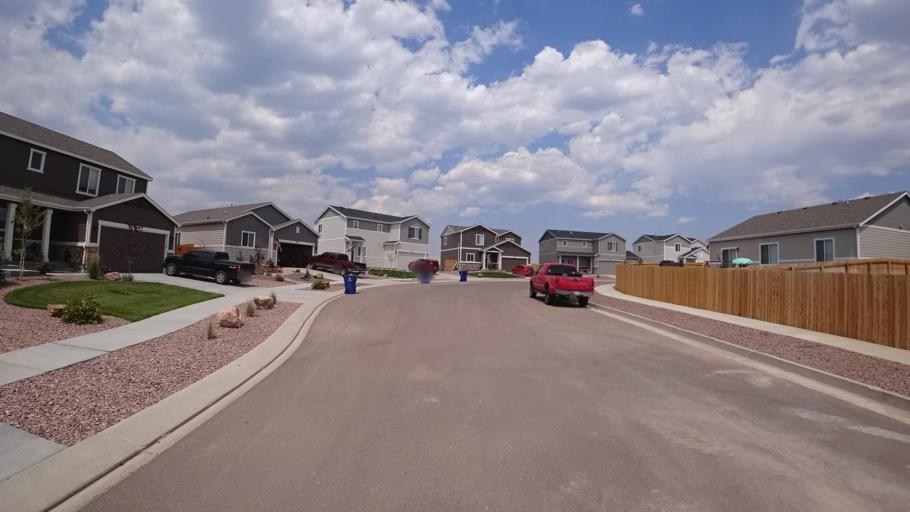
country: US
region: Colorado
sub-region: El Paso County
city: Black Forest
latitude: 38.9472
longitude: -104.6884
